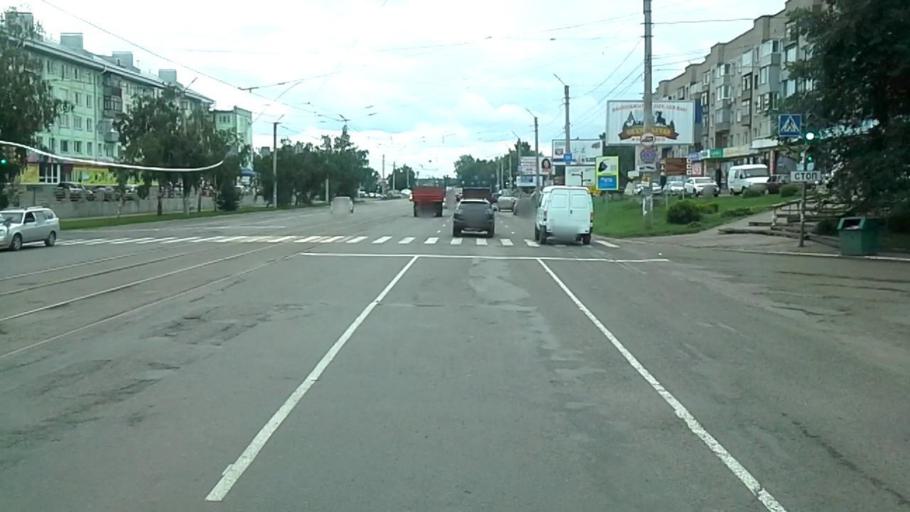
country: RU
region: Altai Krai
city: Biysk
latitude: 52.5431
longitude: 85.2179
